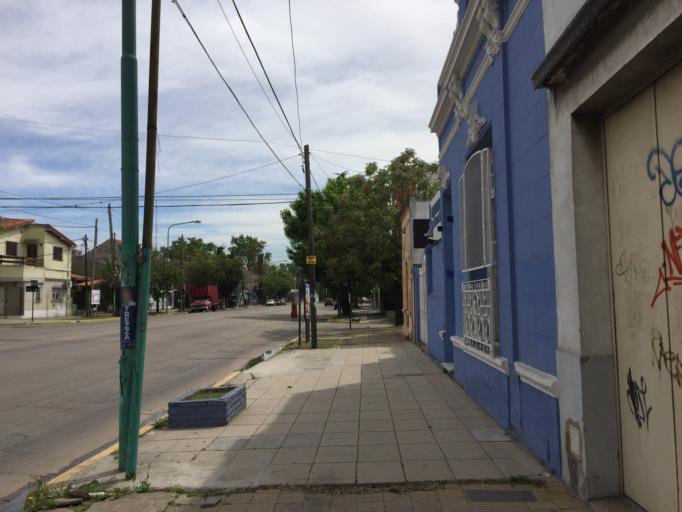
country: AR
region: Buenos Aires
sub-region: Partido de Lomas de Zamora
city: Lomas de Zamora
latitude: -34.7379
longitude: -58.3921
